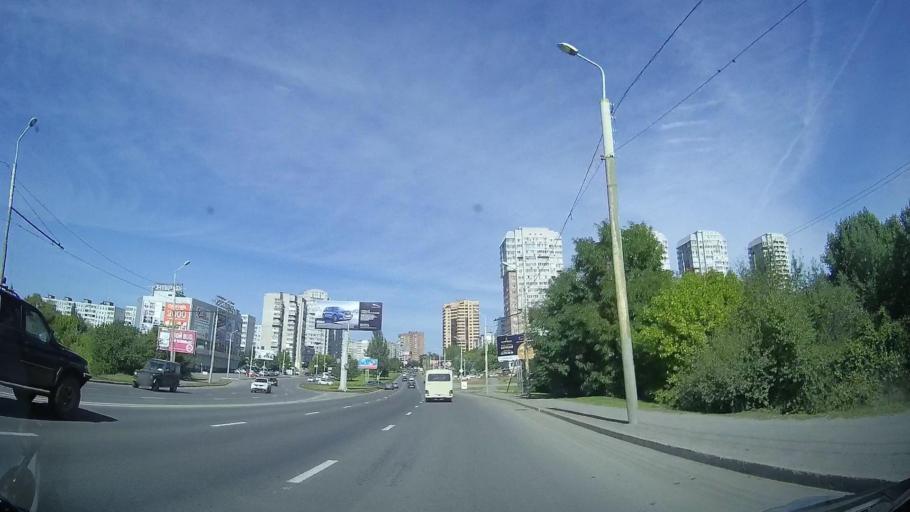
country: RU
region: Rostov
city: Severnyy
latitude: 47.2867
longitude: 39.6943
